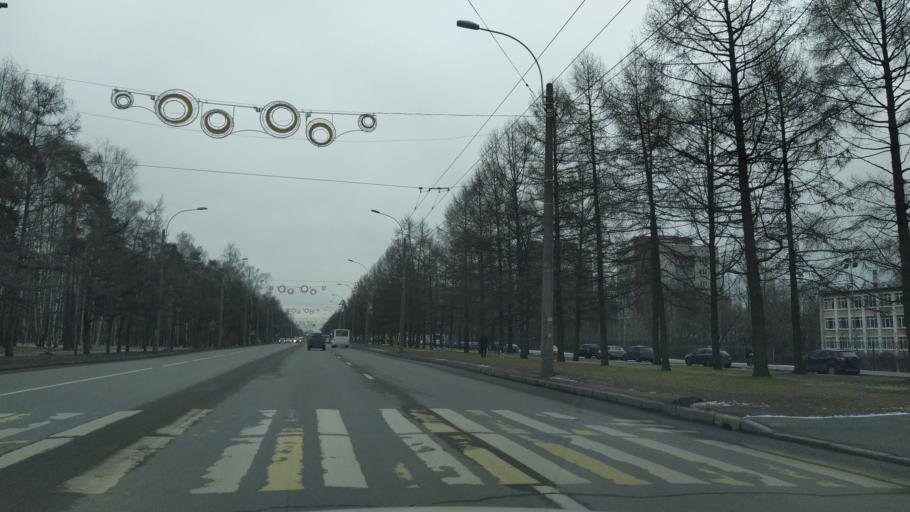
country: RU
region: St.-Petersburg
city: Sosnovka
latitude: 60.0186
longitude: 30.3346
